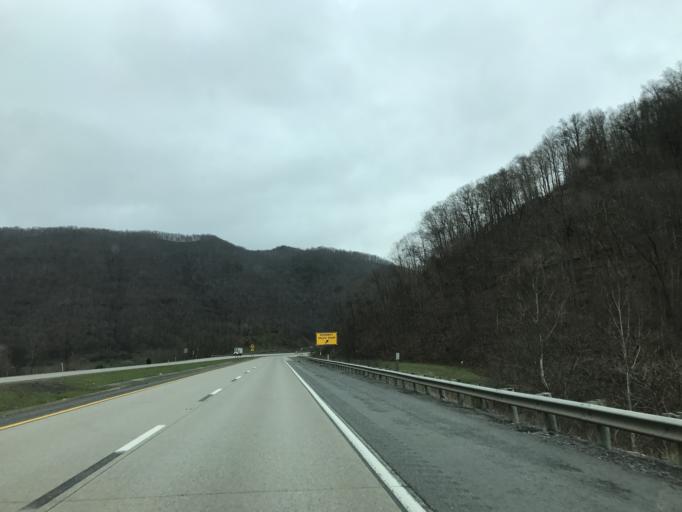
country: US
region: West Virginia
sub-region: Summers County
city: Hinton
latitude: 37.7826
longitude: -80.9204
